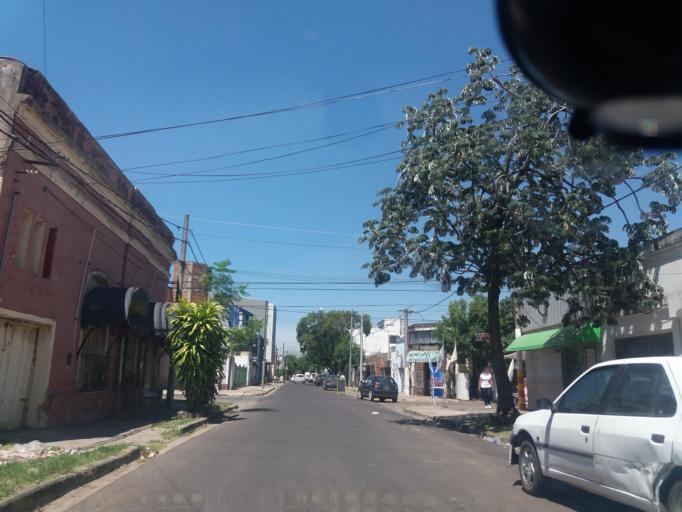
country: AR
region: Corrientes
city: Corrientes
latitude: -27.4770
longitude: -58.8446
